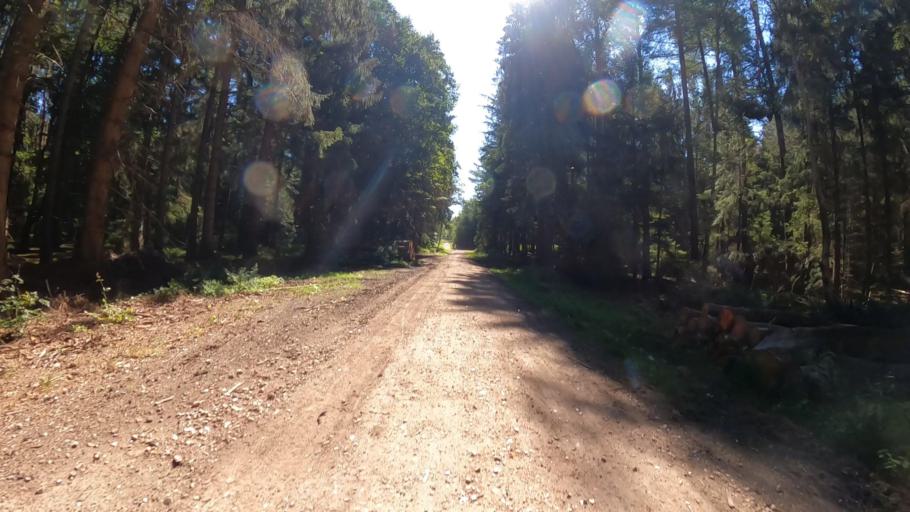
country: DE
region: Schleswig-Holstein
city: Aumuhle
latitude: 53.5145
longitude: 10.3399
